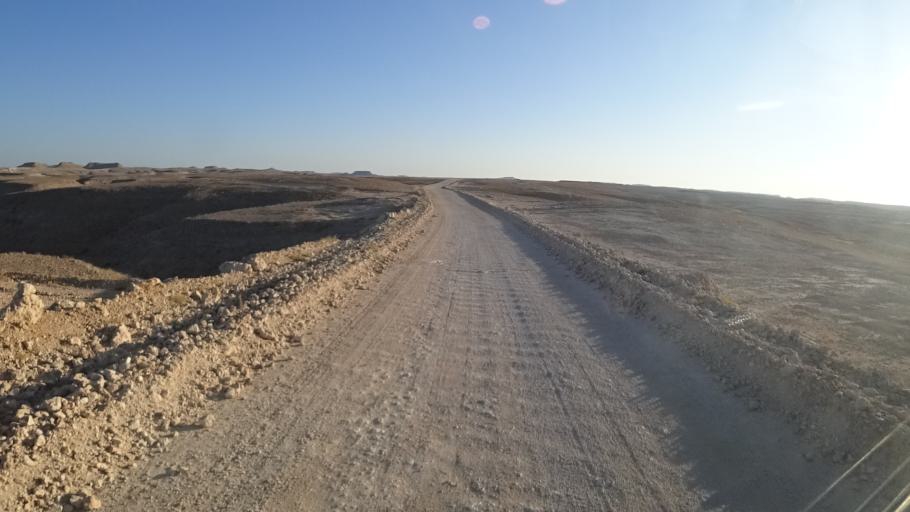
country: YE
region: Al Mahrah
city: Hawf
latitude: 17.1617
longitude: 53.3509
